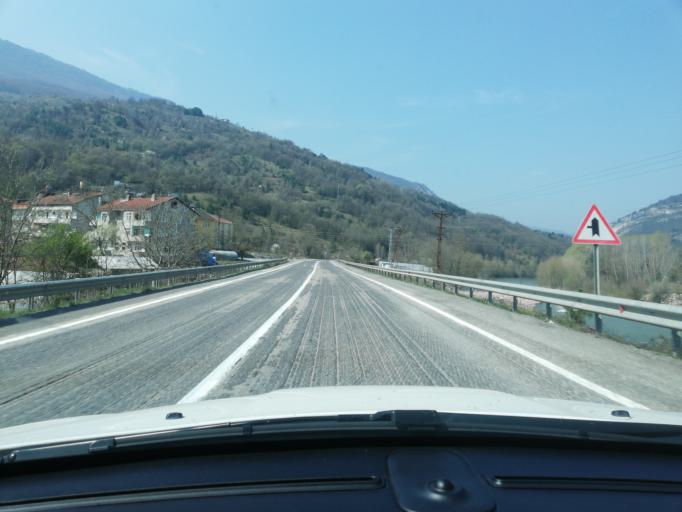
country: TR
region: Karabuk
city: Yenice
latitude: 41.2149
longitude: 32.2551
